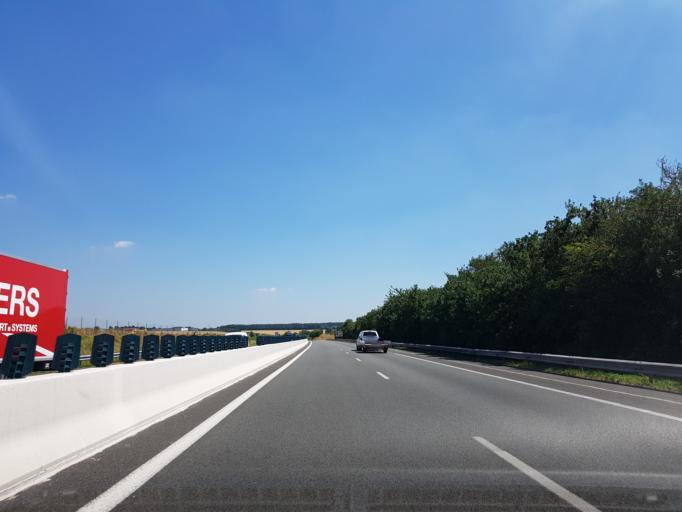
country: FR
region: Nord-Pas-de-Calais
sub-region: Departement du Nord
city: Fontaine-Notre-Dame
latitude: 50.1581
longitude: 3.1620
